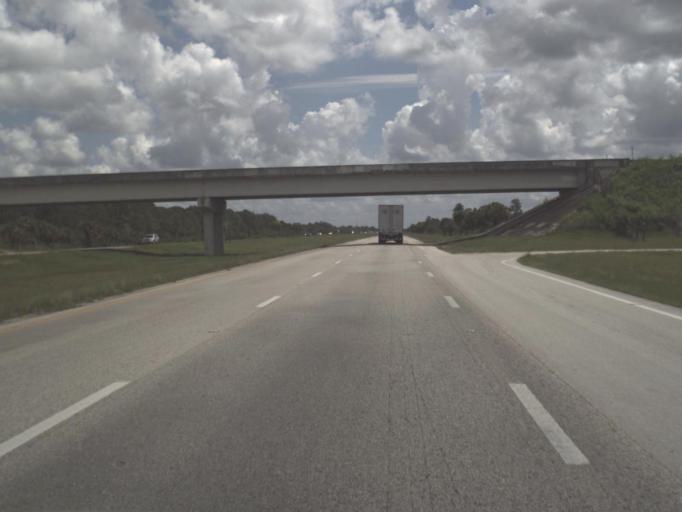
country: US
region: Florida
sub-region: Collier County
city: Orangetree
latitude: 26.1527
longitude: -81.5446
